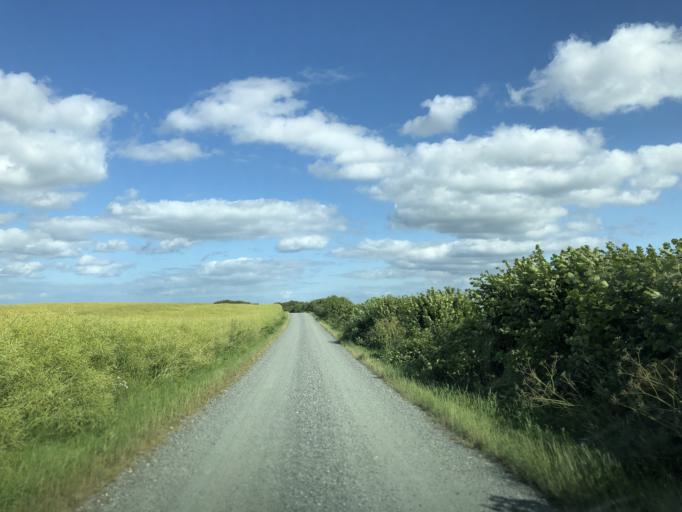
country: DK
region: South Denmark
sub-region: Vejle Kommune
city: Brejning
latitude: 55.6730
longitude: 9.6543
